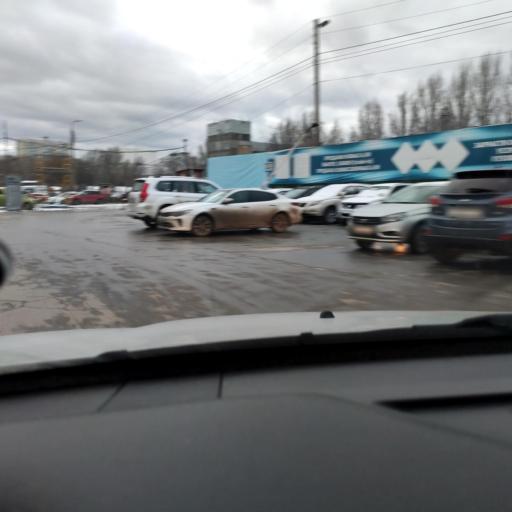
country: RU
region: Samara
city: Samara
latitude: 53.2396
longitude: 50.2446
